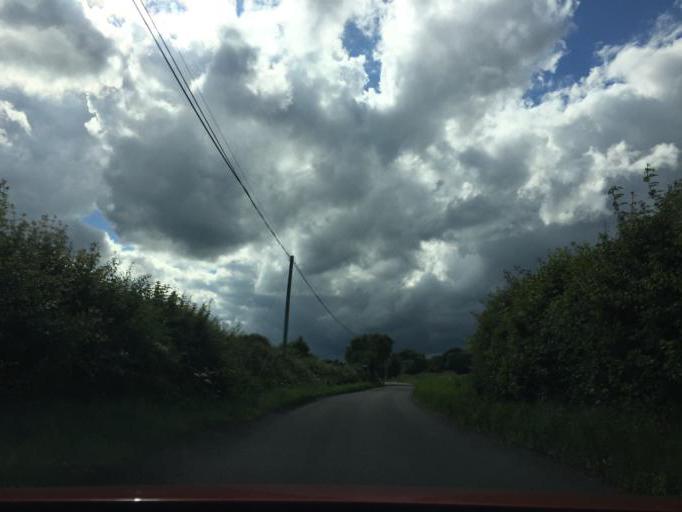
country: GB
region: England
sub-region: Hertfordshire
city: Harpenden
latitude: 51.8535
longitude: -0.3236
